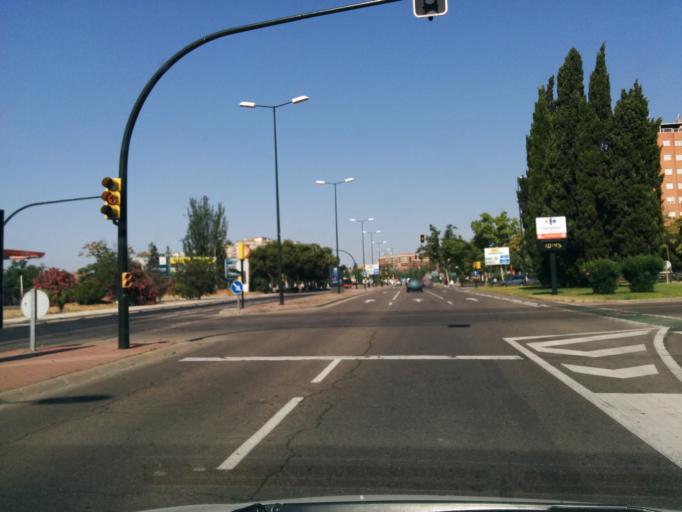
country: ES
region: Aragon
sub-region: Provincia de Zaragoza
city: Zaragoza
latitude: 41.6667
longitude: -0.8763
